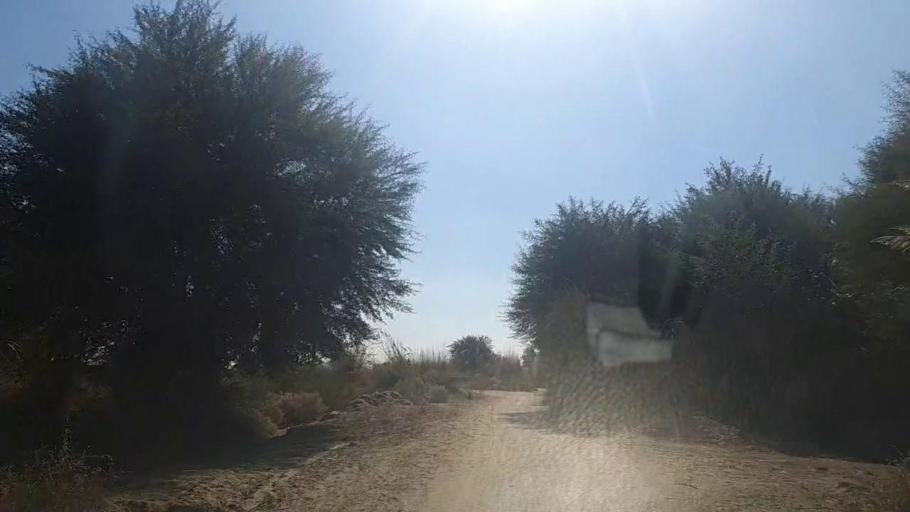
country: PK
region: Sindh
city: Khadro
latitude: 26.1487
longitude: 68.8380
